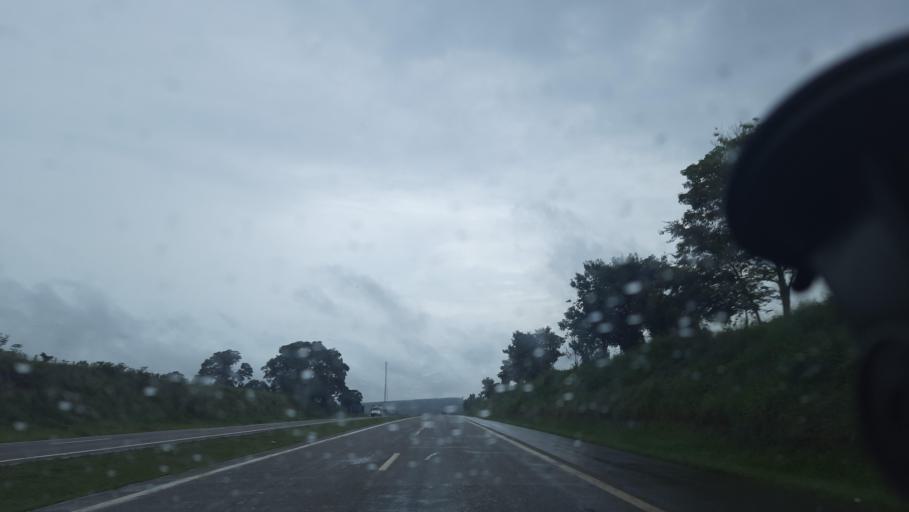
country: BR
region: Sao Paulo
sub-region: Casa Branca
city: Casa Branca
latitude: -21.8143
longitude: -47.0640
